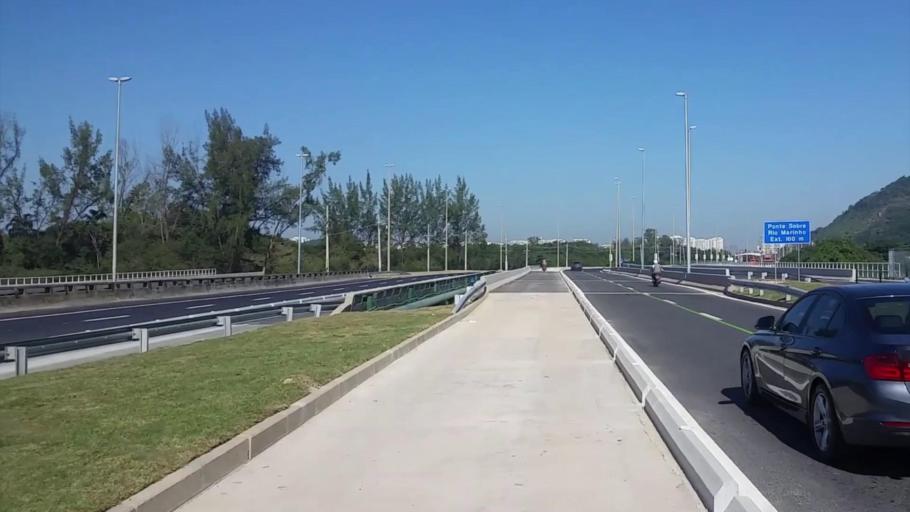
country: BR
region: Rio de Janeiro
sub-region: Nilopolis
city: Nilopolis
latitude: -22.9790
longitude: -43.4080
